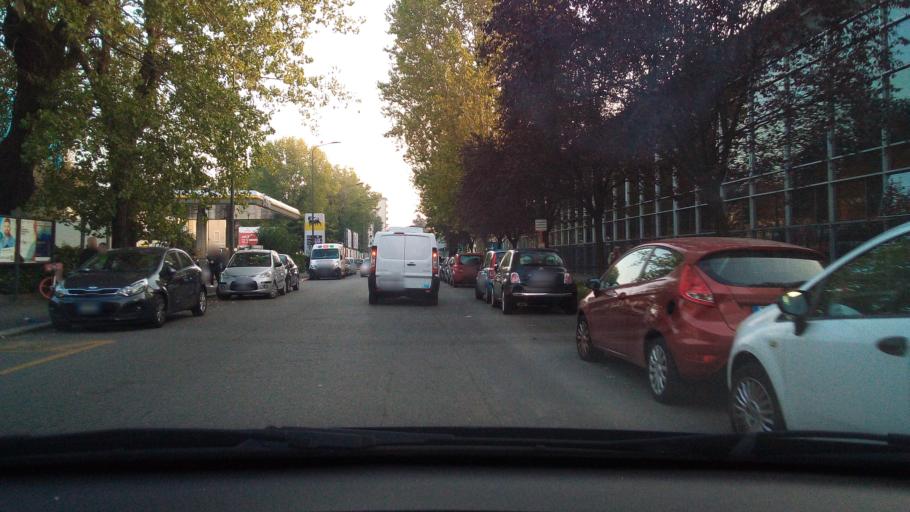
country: IT
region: Lombardy
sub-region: Citta metropolitana di Milano
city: Sesto San Giovanni
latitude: 45.5013
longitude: 9.2285
